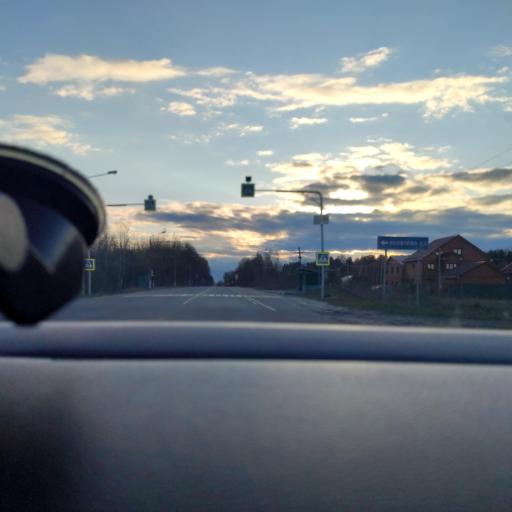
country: RU
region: Moskovskaya
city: Krasnyy Tkach
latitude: 55.4285
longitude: 39.2150
